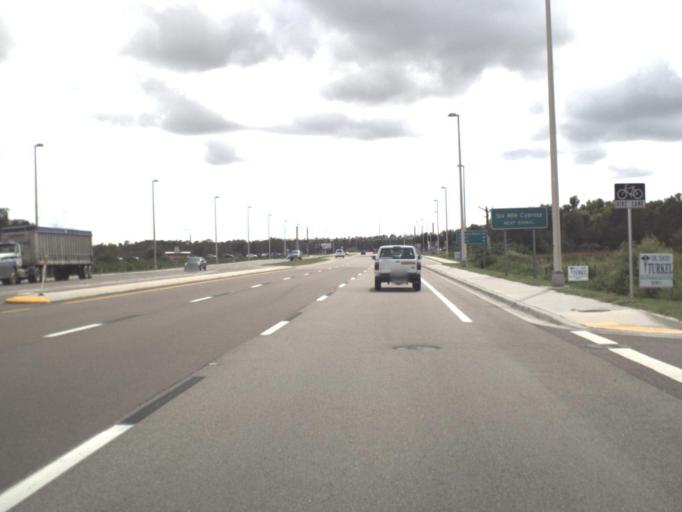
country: US
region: Florida
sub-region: Lee County
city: Villas
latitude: 26.5320
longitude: -81.8528
